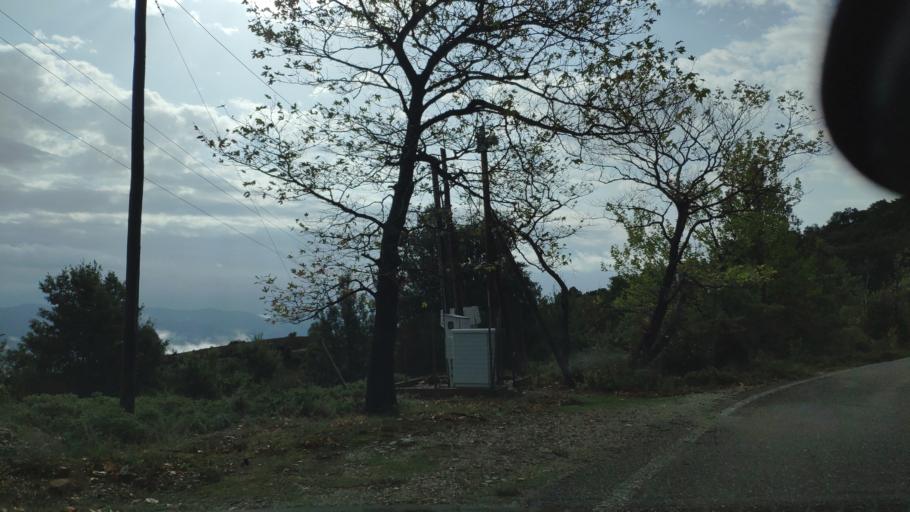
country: GR
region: West Greece
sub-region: Nomos Aitolias kai Akarnanias
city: Sardinia
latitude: 38.8638
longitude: 21.3011
